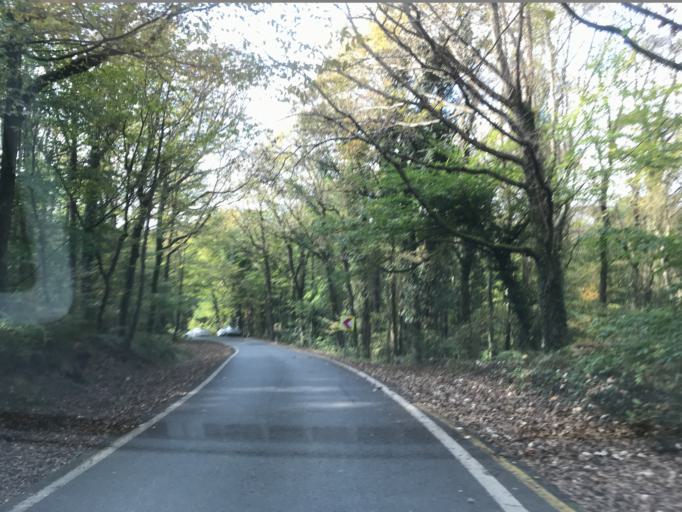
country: TR
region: Istanbul
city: Arikoey
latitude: 41.1895
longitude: 28.9711
